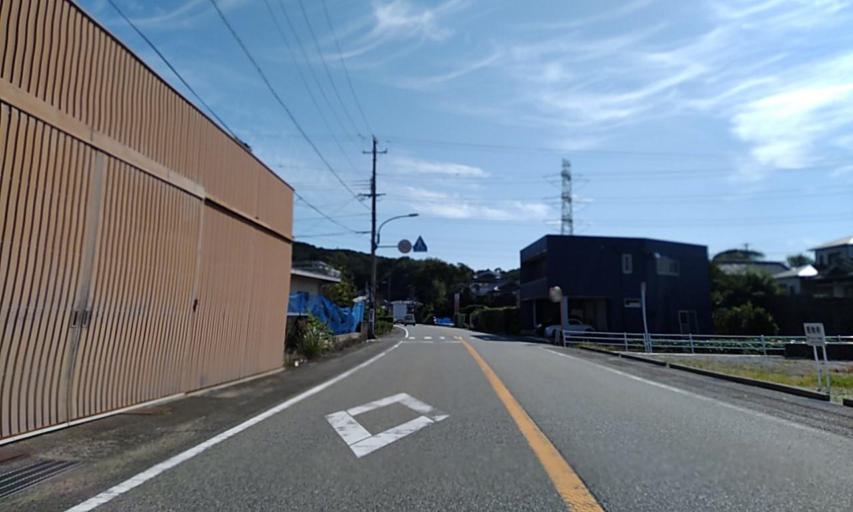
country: JP
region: Wakayama
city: Gobo
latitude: 33.8625
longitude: 135.1615
